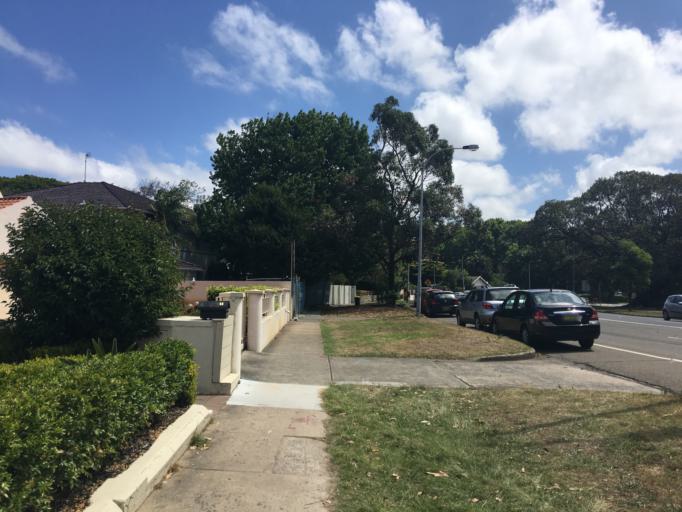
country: AU
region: New South Wales
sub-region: Woollahra
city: Bellevue Hill
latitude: -33.8725
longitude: 151.2641
